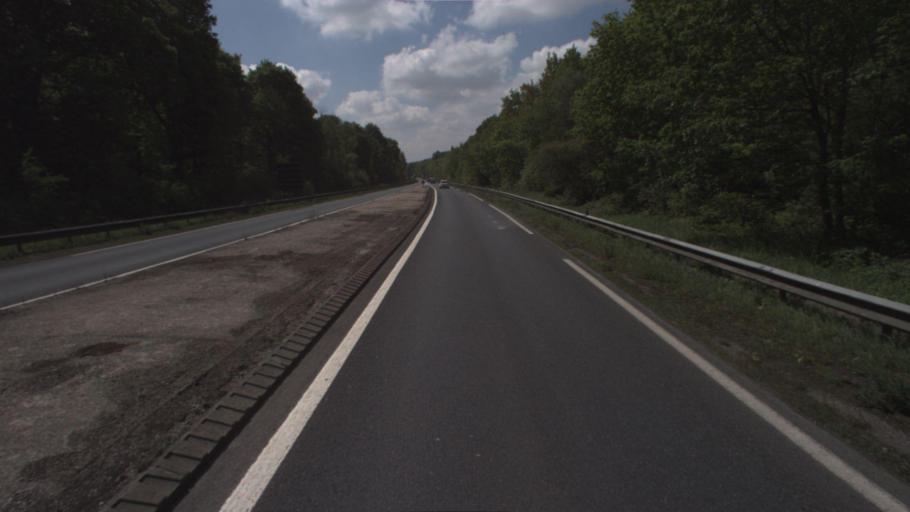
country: FR
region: Ile-de-France
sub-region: Departement de Seine-et-Marne
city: Chaumes-en-Brie
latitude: 48.6927
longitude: 2.8197
